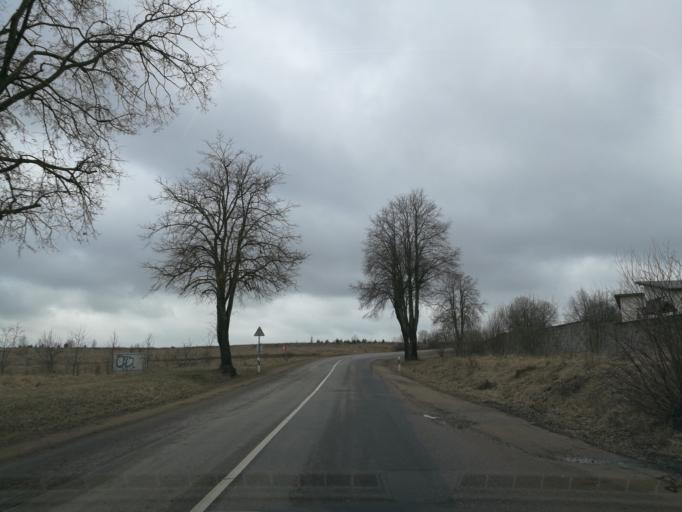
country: LT
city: Grigiskes
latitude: 54.6442
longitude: 25.0908
